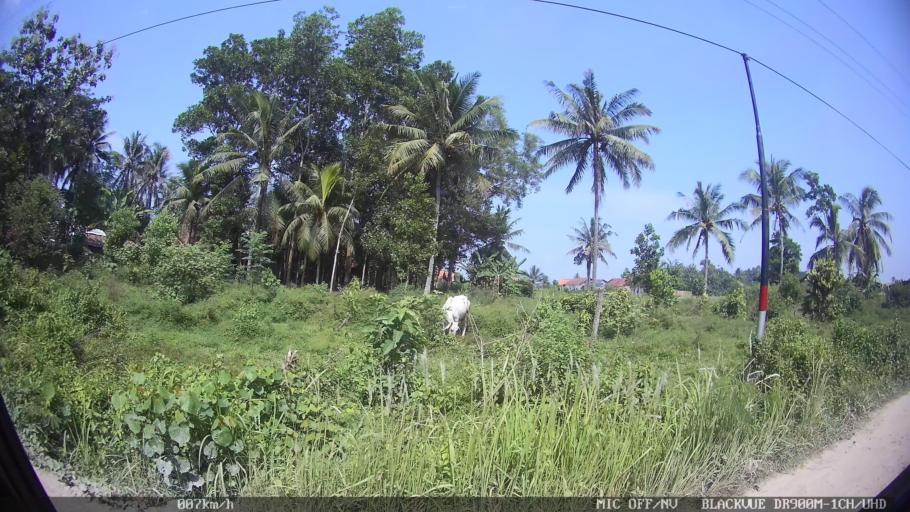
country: ID
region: Lampung
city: Natar
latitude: -5.2599
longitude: 105.1973
